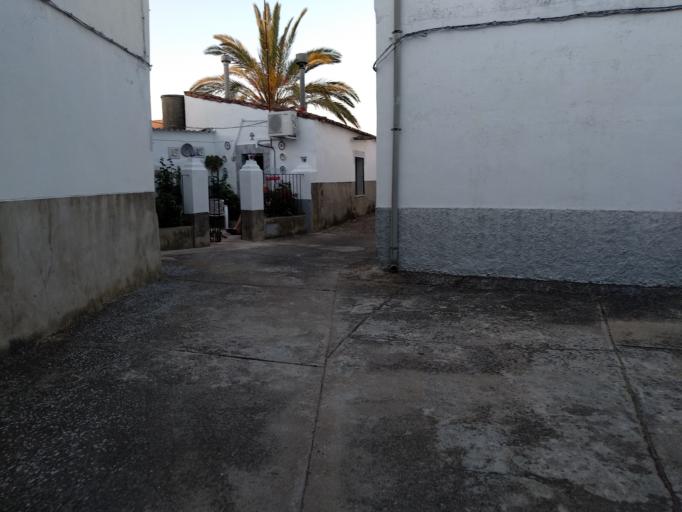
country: ES
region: Extremadura
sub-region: Provincia de Caceres
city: Albala
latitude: 39.2570
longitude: -6.1843
